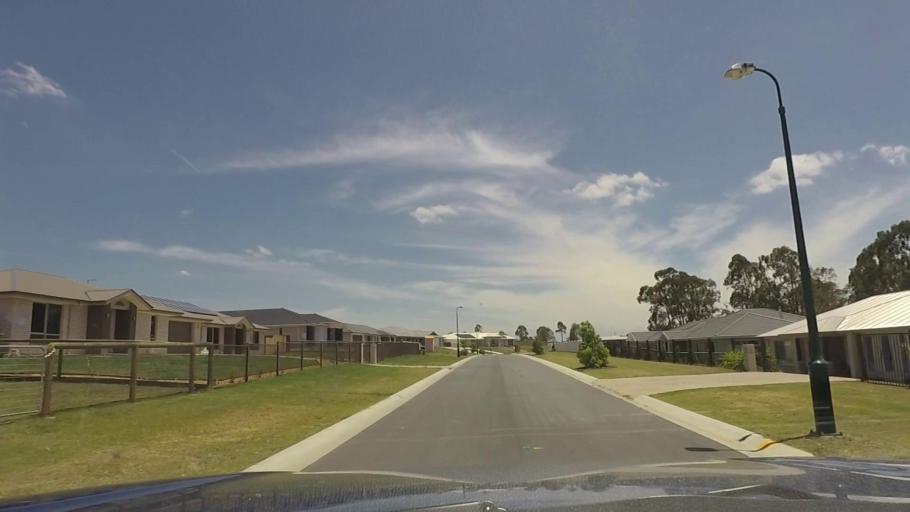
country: AU
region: Queensland
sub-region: Logan
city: Chambers Flat
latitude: -27.7688
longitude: 153.0904
